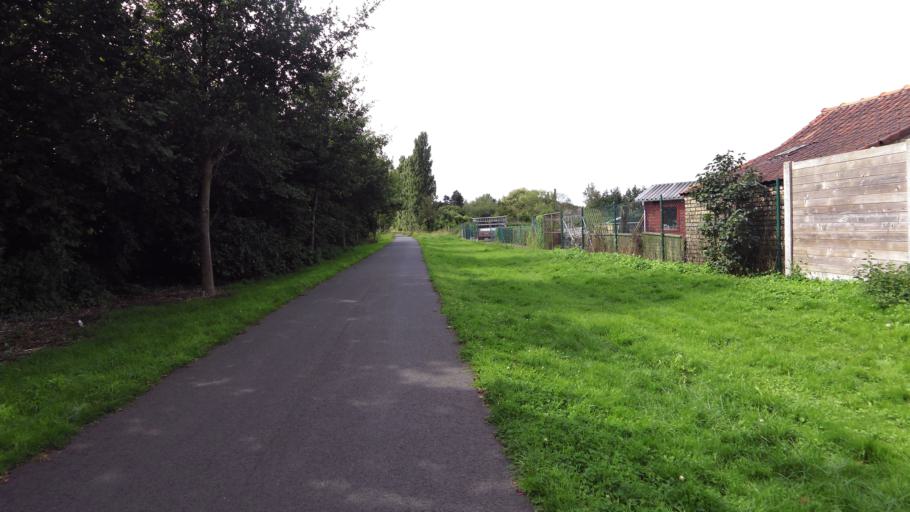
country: BE
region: Flanders
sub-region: Provincie West-Vlaanderen
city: Ichtegem
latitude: 51.1272
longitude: 3.0197
